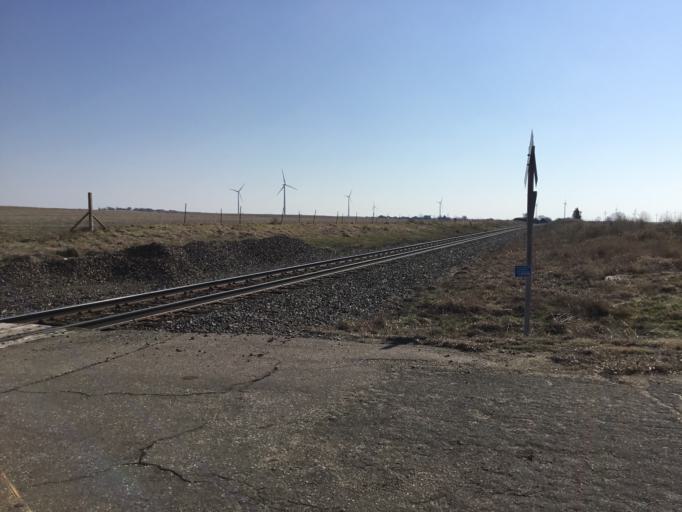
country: US
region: Kansas
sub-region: Ellsworth County
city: Ellsworth
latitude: 38.8143
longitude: -98.4308
